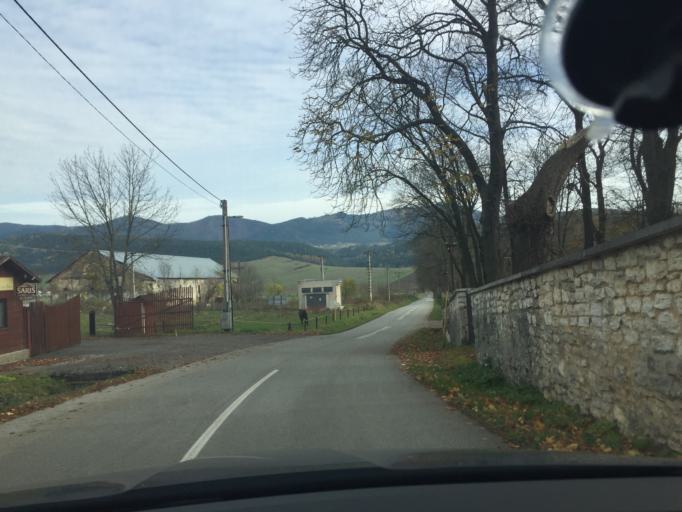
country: SK
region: Presovsky
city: Spisske Podhradie
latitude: 48.9894
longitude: 20.7834
